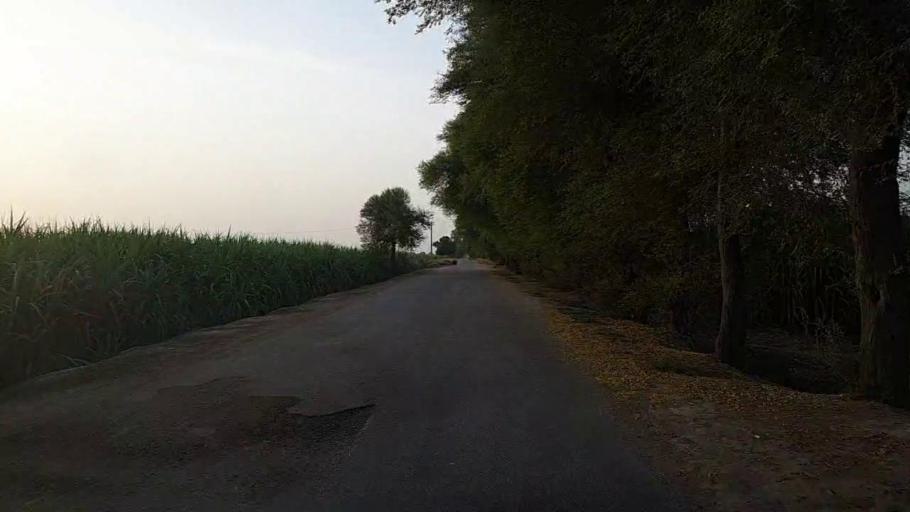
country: PK
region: Sindh
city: Ubauro
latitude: 28.2425
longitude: 69.8113
